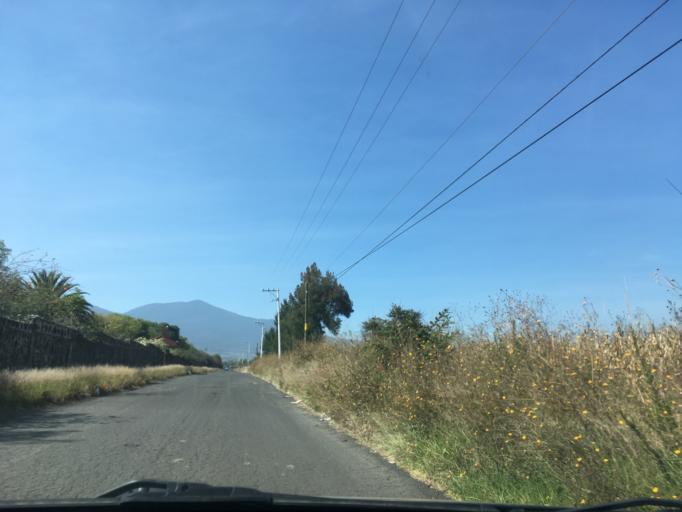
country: MX
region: Michoacan
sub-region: Morelia
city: La Mintzita (Piedra Dura)
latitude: 19.6497
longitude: -101.2869
